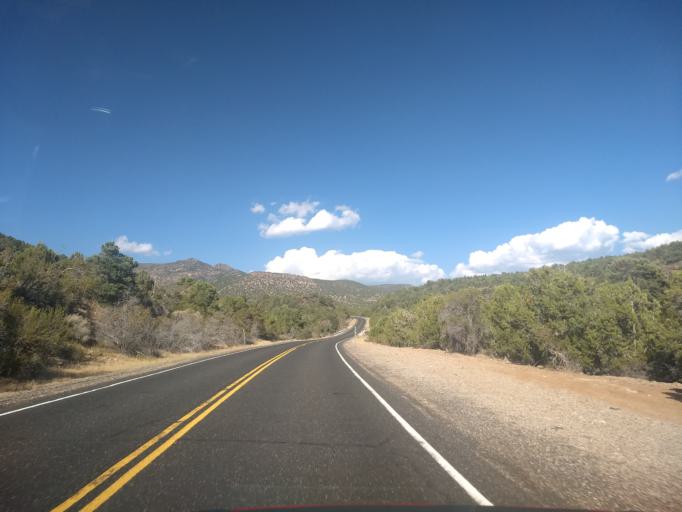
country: US
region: Utah
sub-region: Washington County
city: Enterprise
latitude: 37.4185
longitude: -113.5965
